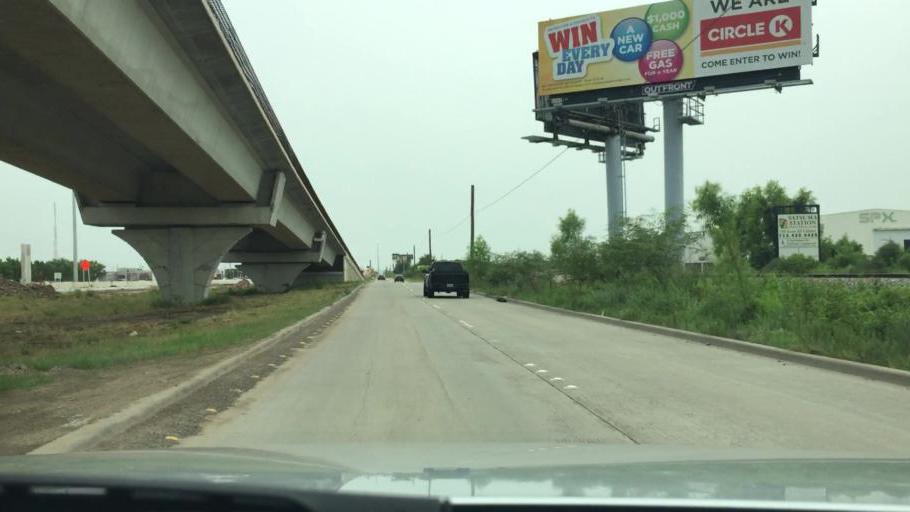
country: US
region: Texas
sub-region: Harris County
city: Oak Cliff Place
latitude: 29.9078
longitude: -95.6097
